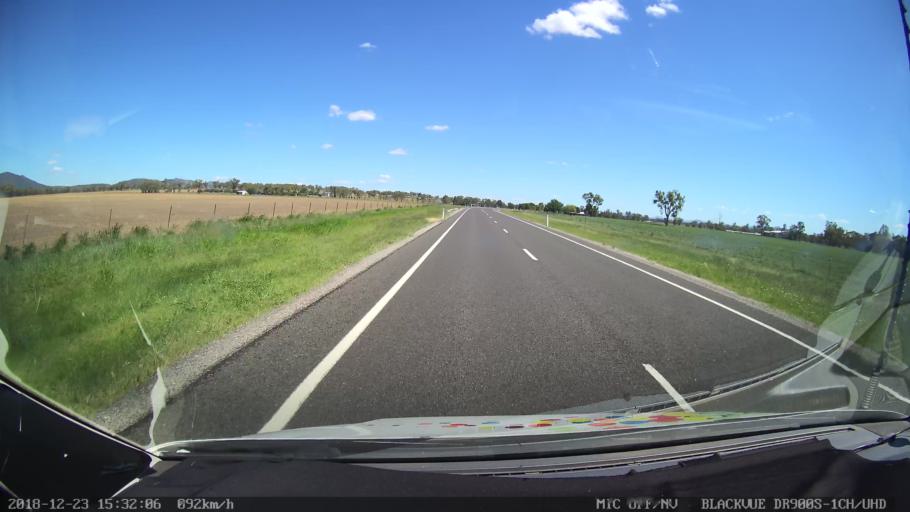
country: AU
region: New South Wales
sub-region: Tamworth Municipality
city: East Tamworth
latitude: -30.9812
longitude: 150.8701
